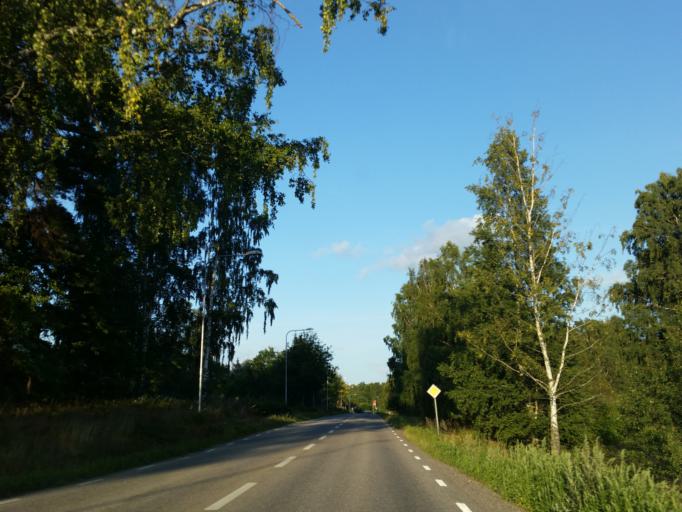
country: SE
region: Stockholm
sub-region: Nykvarns Kommun
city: Nykvarn
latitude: 59.2523
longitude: 17.5162
